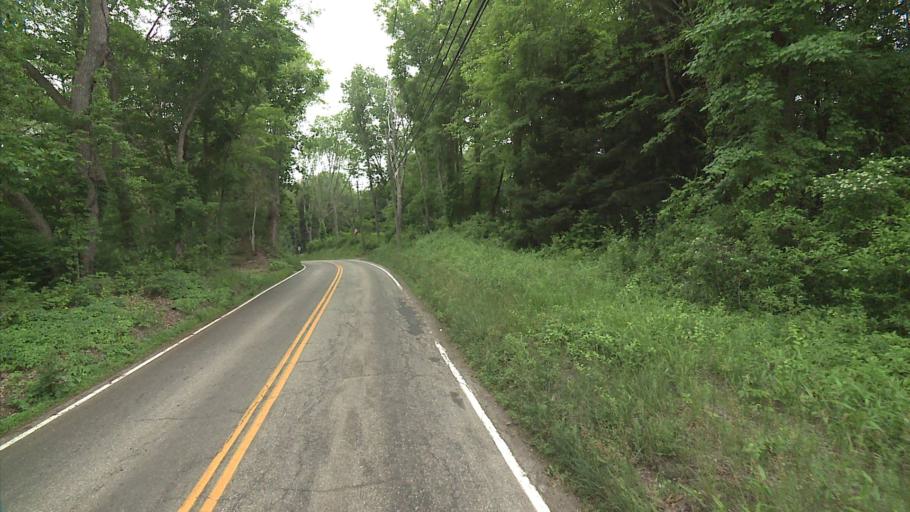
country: US
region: Connecticut
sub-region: Tolland County
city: Coventry Lake
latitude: 41.7298
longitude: -72.3705
